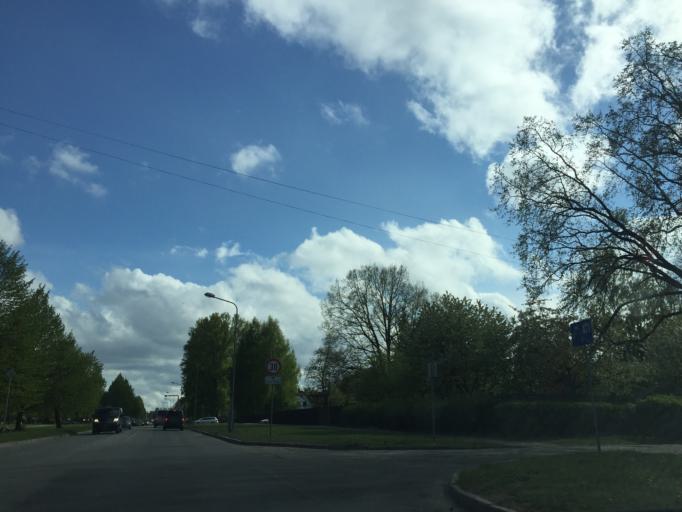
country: LV
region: Riga
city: Riga
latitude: 56.9377
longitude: 24.1950
